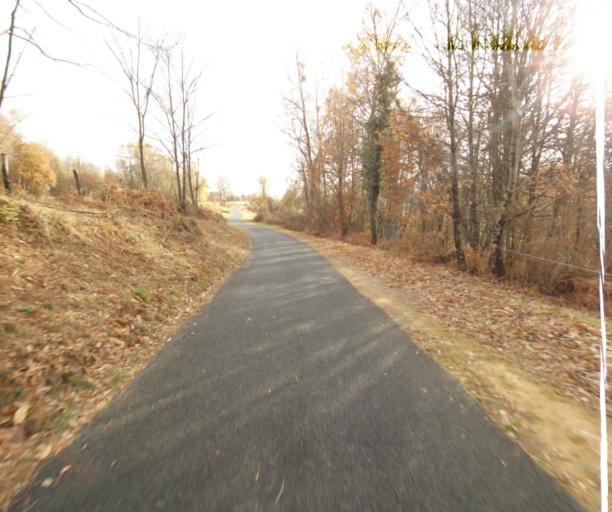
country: FR
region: Limousin
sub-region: Departement de la Correze
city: Sainte-Fortunade
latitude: 45.1830
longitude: 1.7905
